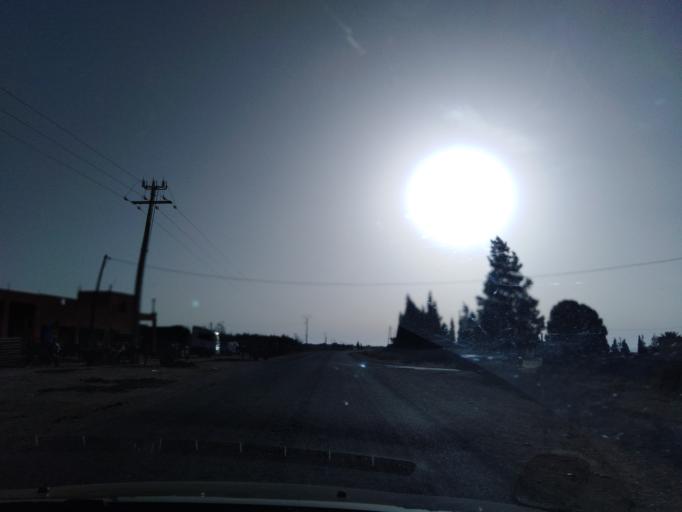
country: MA
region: Doukkala-Abda
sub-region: Safi
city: Safi
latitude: 32.4781
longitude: -8.8812
